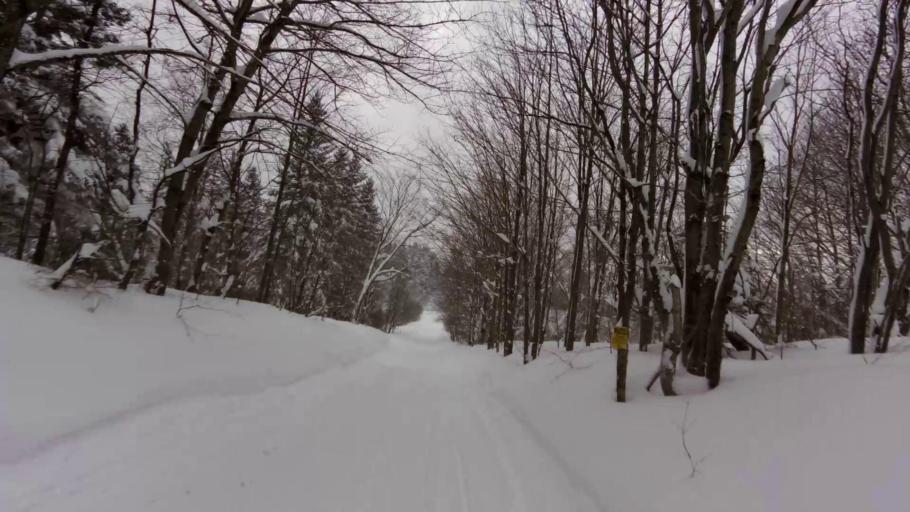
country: US
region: New York
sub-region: Lewis County
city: Lowville
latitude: 43.7328
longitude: -75.6513
